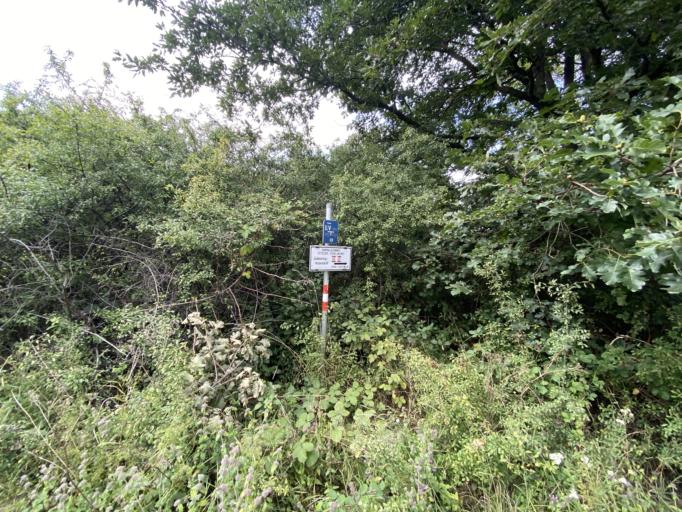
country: AT
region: Burgenland
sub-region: Politischer Bezirk Oberpullendorf
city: Kaisersdorf
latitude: 47.5635
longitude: 16.3474
